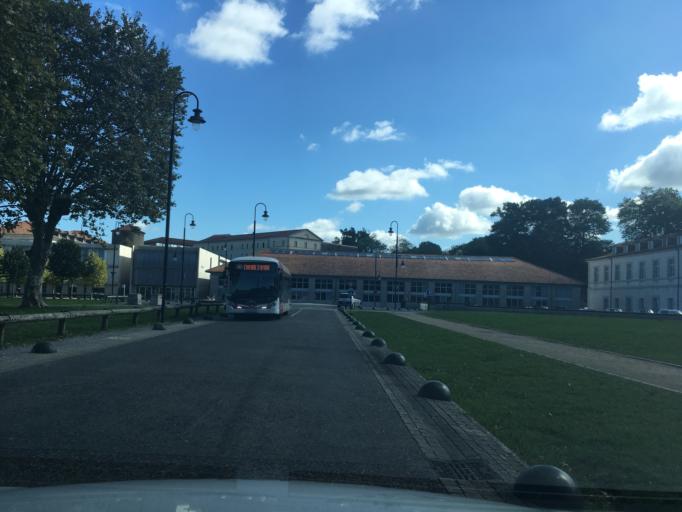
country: FR
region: Aquitaine
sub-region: Departement des Pyrenees-Atlantiques
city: Bayonne
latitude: 43.4881
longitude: -1.4732
